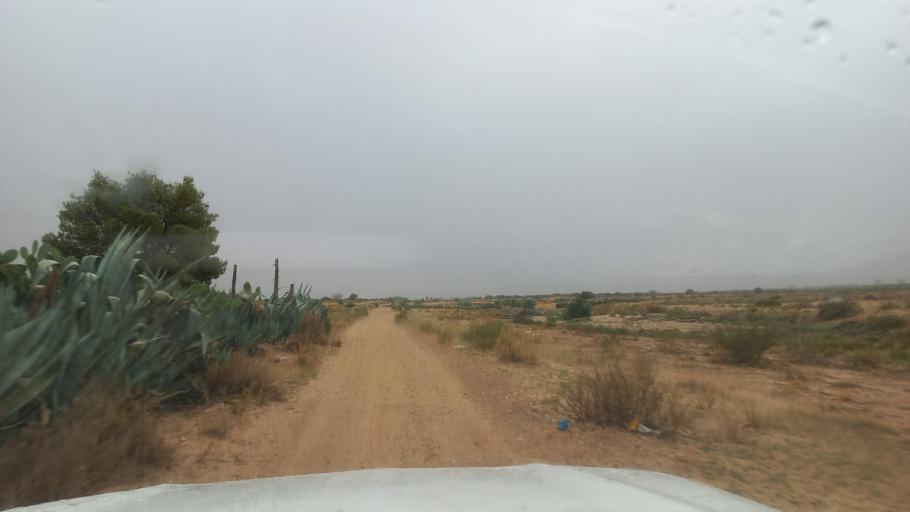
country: TN
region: Al Qasrayn
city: Kasserine
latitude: 35.2691
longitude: 8.9469
